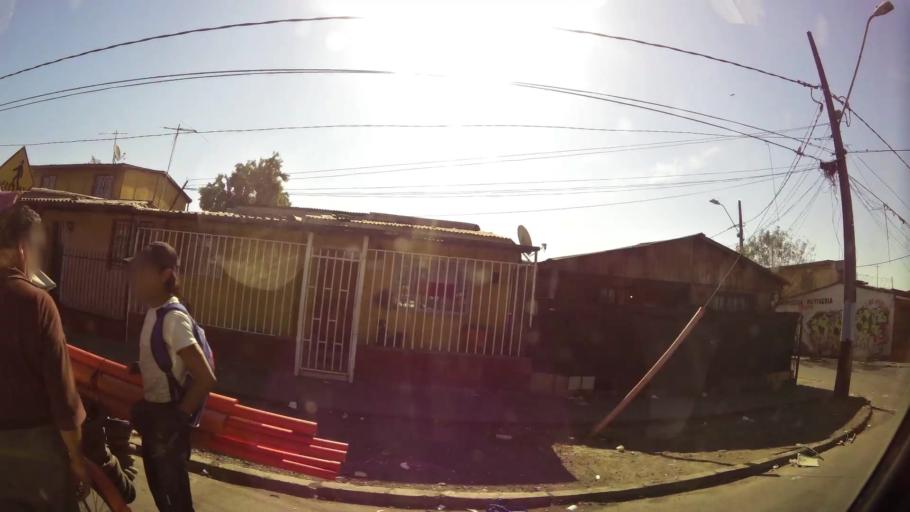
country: CL
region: Santiago Metropolitan
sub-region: Provincia de Santiago
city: Santiago
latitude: -33.5133
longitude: -70.6862
